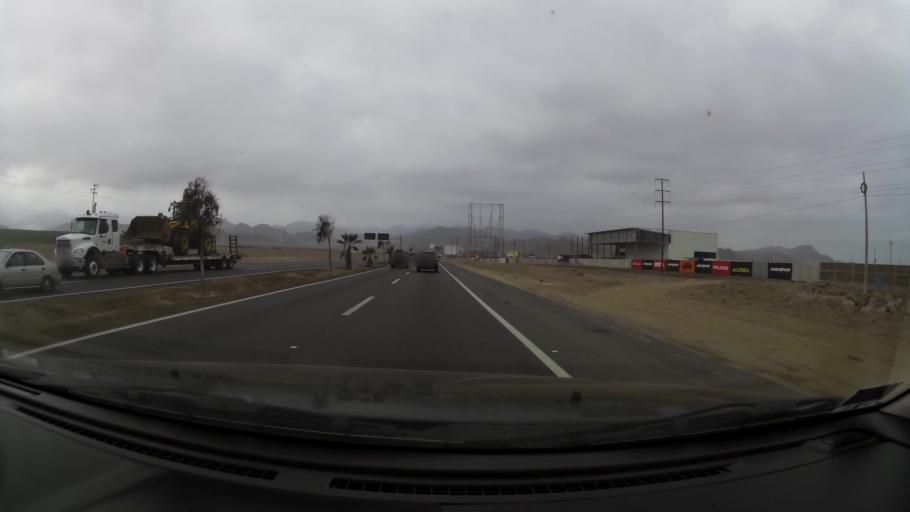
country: PE
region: Lima
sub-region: Lima
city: San Bartolo
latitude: -12.3814
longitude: -76.7743
